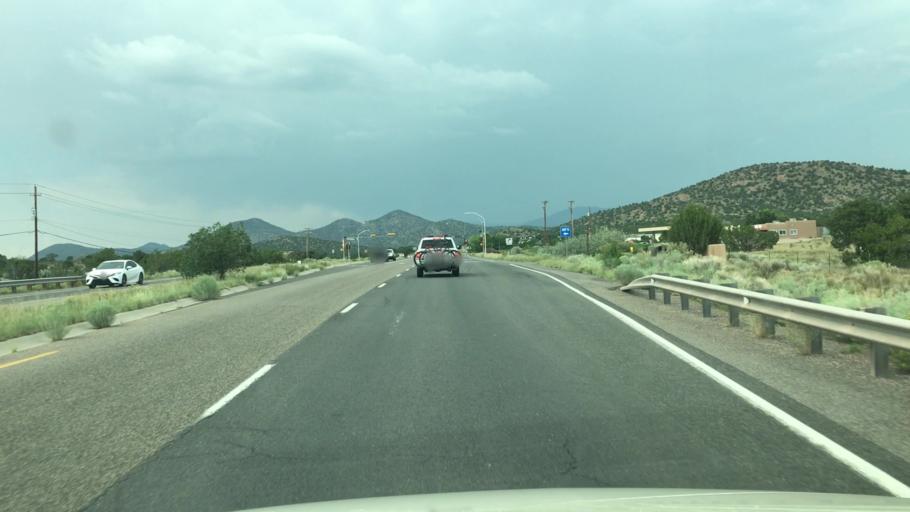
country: US
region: New Mexico
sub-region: Santa Fe County
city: Eldorado at Santa Fe
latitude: 35.5348
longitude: -105.8876
